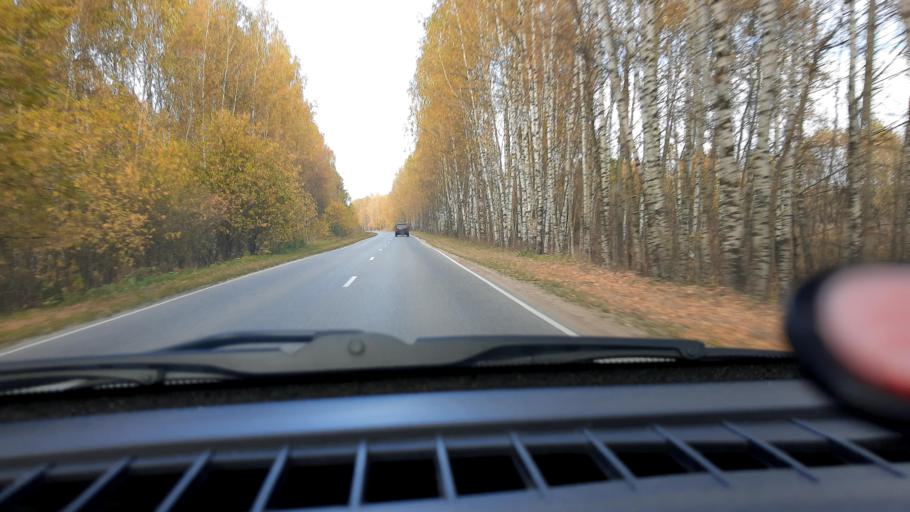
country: RU
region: Nizjnij Novgorod
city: Neklyudovo
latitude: 56.5190
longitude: 43.8370
